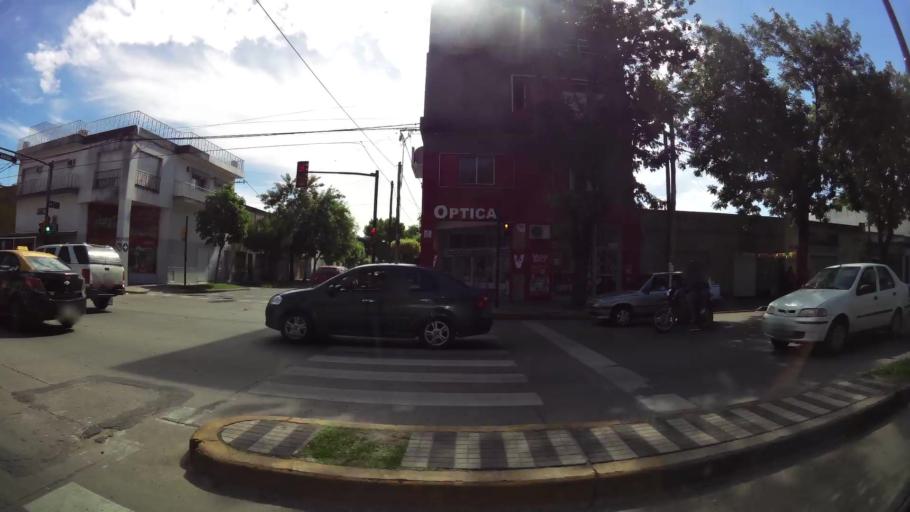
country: AR
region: Santa Fe
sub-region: Departamento de Rosario
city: Rosario
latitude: -32.9379
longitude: -60.7128
